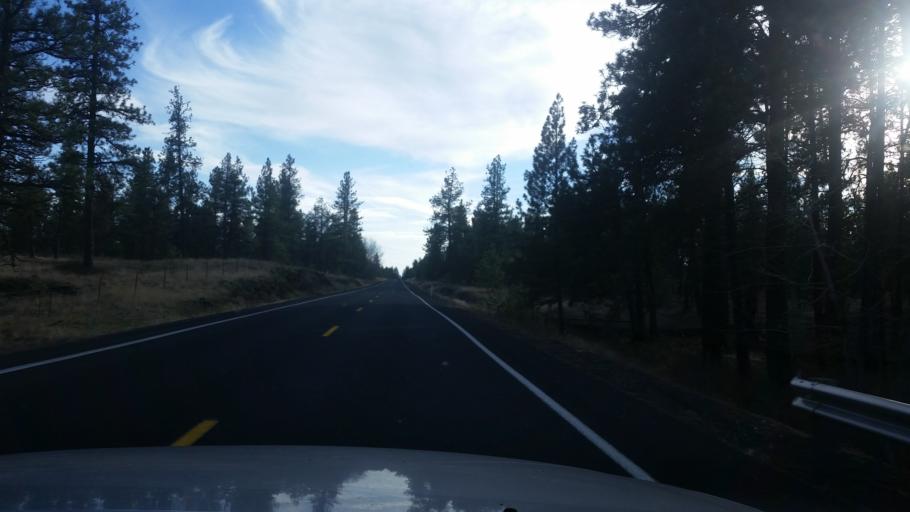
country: US
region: Washington
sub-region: Spokane County
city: Cheney
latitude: 47.4128
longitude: -117.5684
